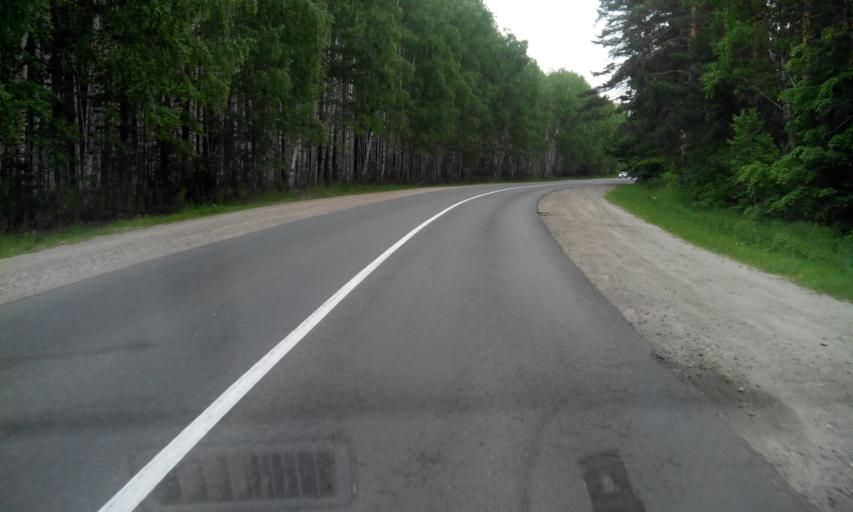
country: RU
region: Penza
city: Zarechnyy
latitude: 53.2136
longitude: 45.1355
